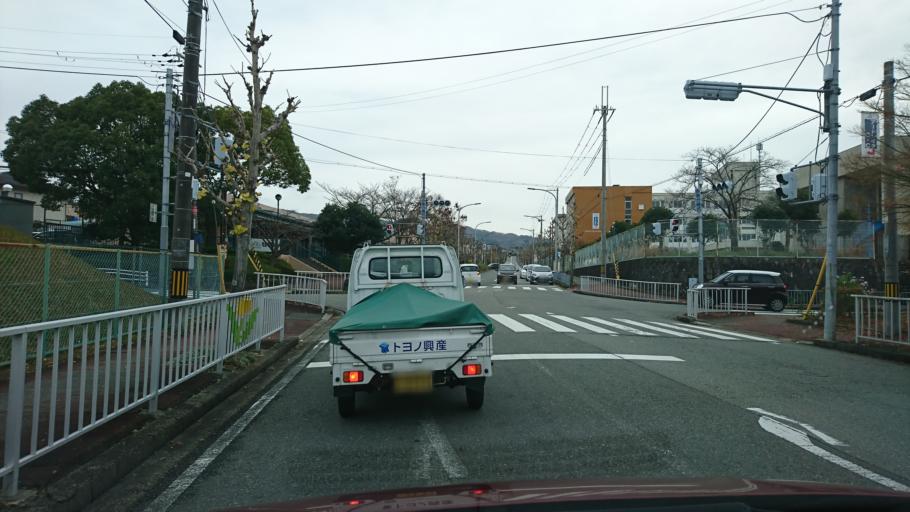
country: JP
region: Osaka
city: Mino
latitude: 34.9026
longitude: 135.4439
